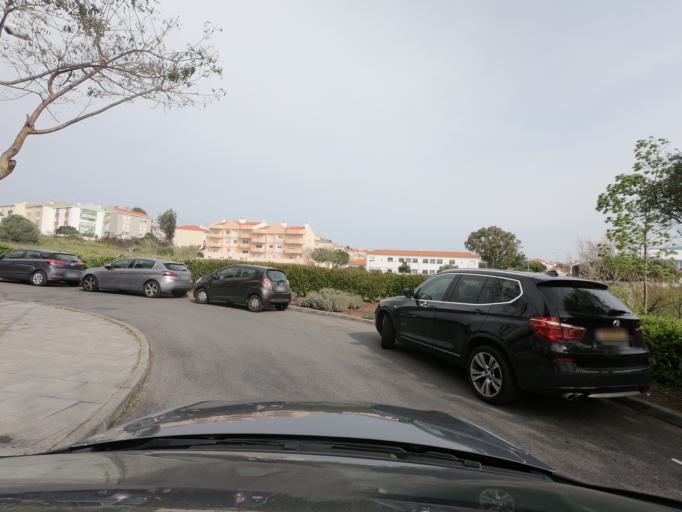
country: PT
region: Lisbon
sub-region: Oeiras
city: Porto Salvo
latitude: 38.7154
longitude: -9.2989
